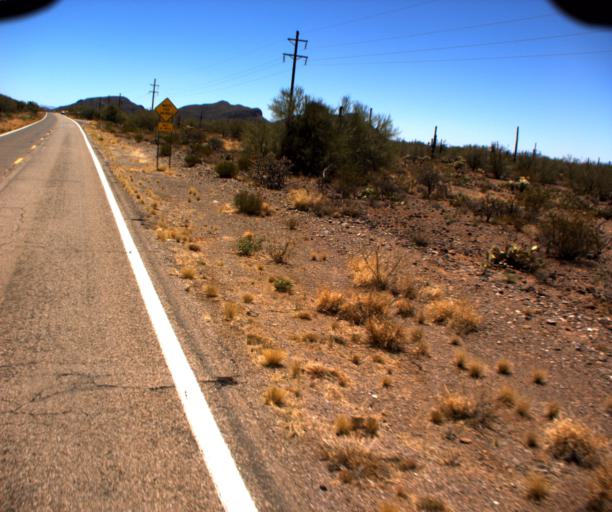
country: US
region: Arizona
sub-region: Pima County
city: Sells
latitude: 31.9848
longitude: -111.9731
